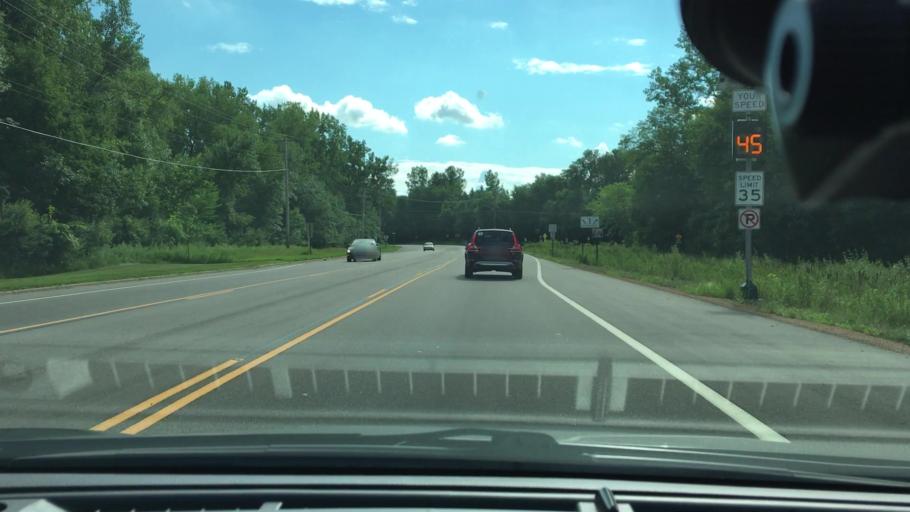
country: US
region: Minnesota
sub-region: Hennepin County
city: Long Lake
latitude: 44.9668
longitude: -93.5562
